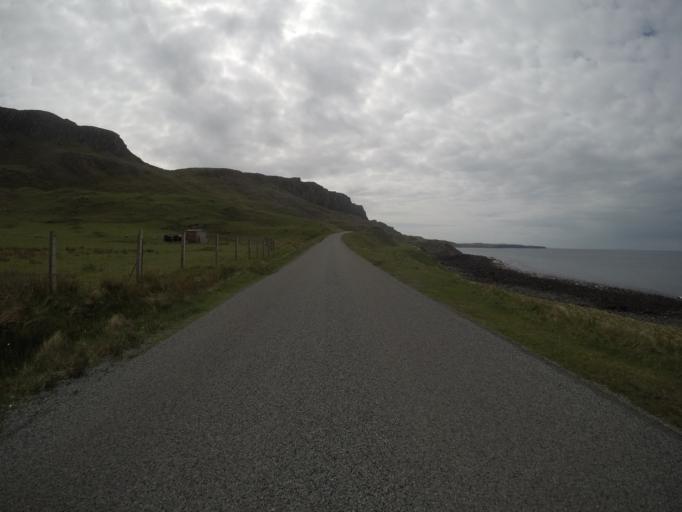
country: GB
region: Scotland
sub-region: Highland
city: Portree
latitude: 57.6774
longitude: -6.3464
